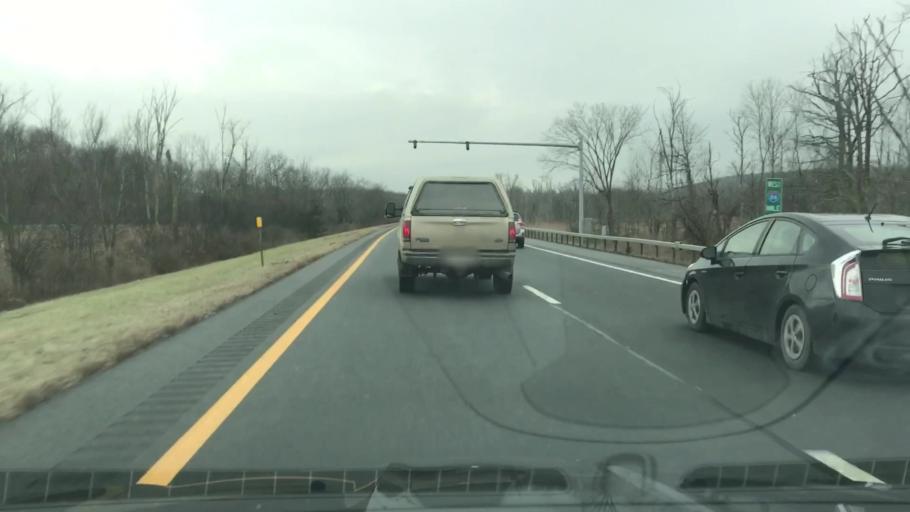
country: US
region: New York
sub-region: Orange County
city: Montgomery
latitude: 41.4817
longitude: -74.2885
